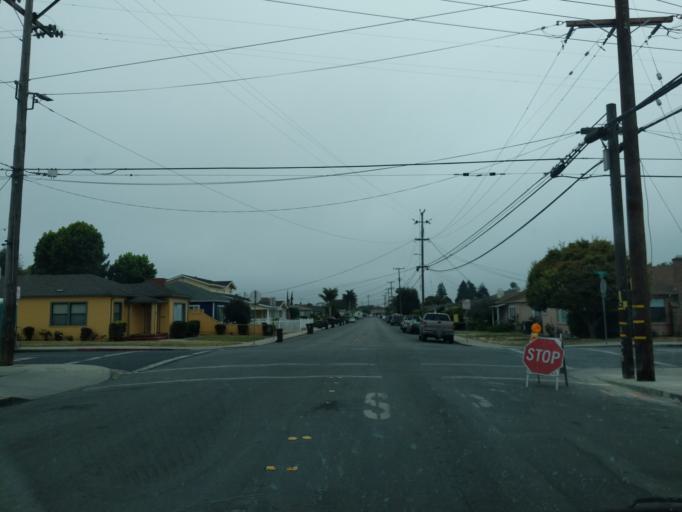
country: US
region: California
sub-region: Santa Cruz County
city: Watsonville
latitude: 36.9166
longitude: -121.7480
